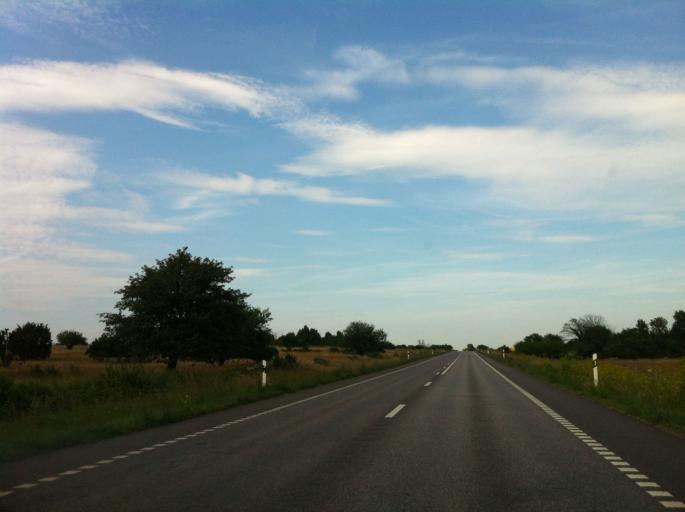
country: SE
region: Kalmar
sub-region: Borgholms Kommun
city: Borgholm
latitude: 56.8393
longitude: 16.6303
